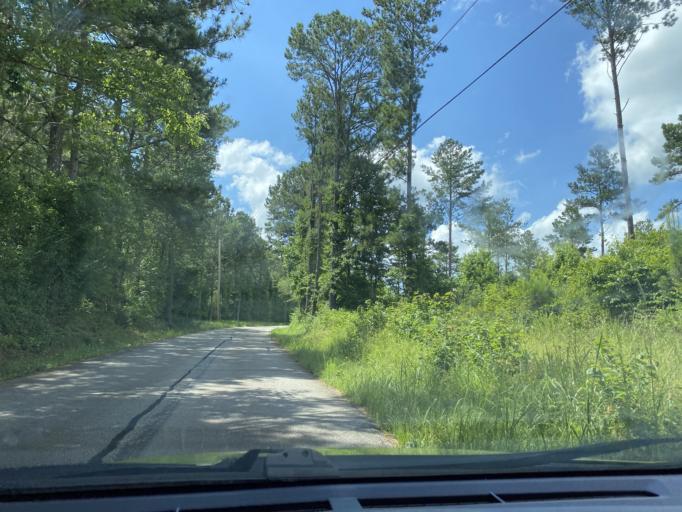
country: US
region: Georgia
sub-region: Fulton County
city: Palmetto
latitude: 33.4252
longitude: -84.7047
